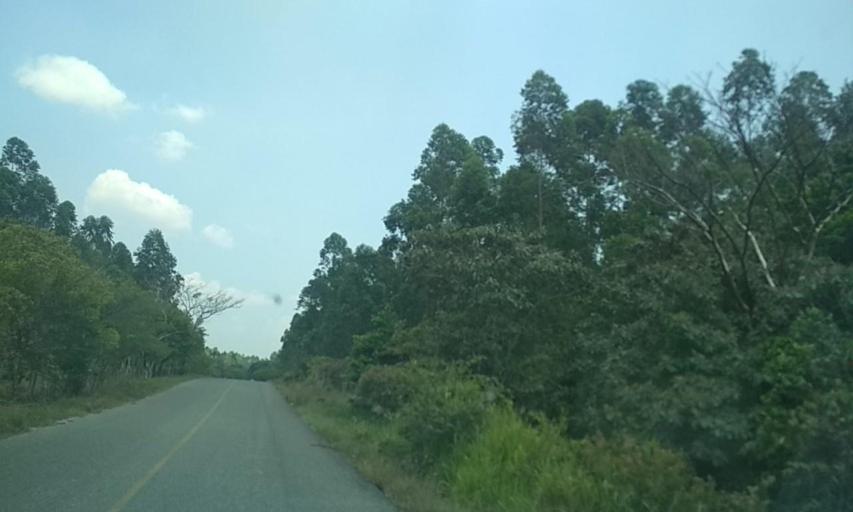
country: MX
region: Tabasco
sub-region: Huimanguillo
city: Francisco Rueda
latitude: 17.8420
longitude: -93.8943
